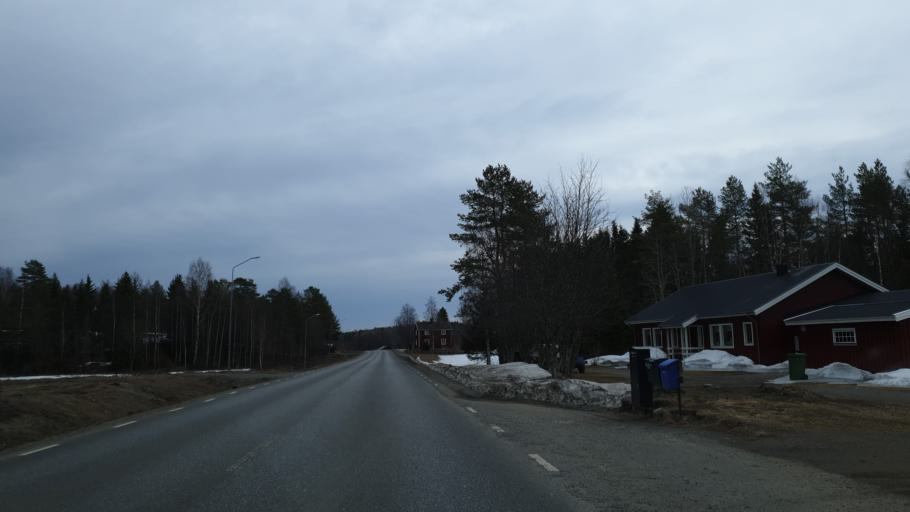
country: SE
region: Vaesterbotten
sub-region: Robertsfors Kommun
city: Robertsfors
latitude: 64.2322
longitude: 20.9929
